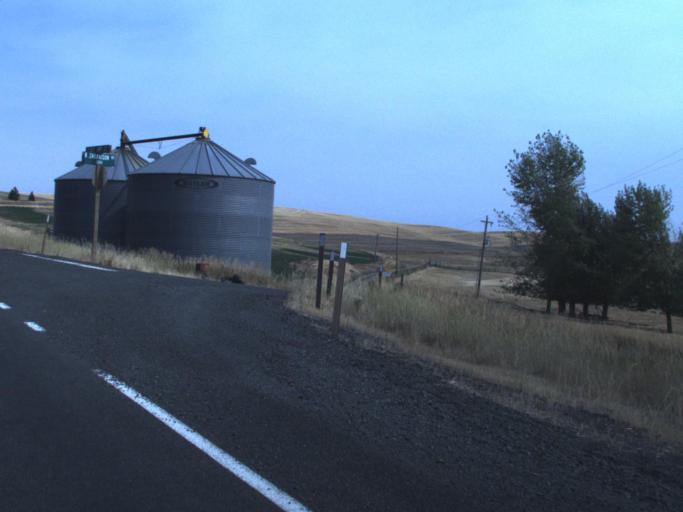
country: US
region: Washington
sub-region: Whitman County
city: Pullman
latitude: 46.8129
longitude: -117.1172
